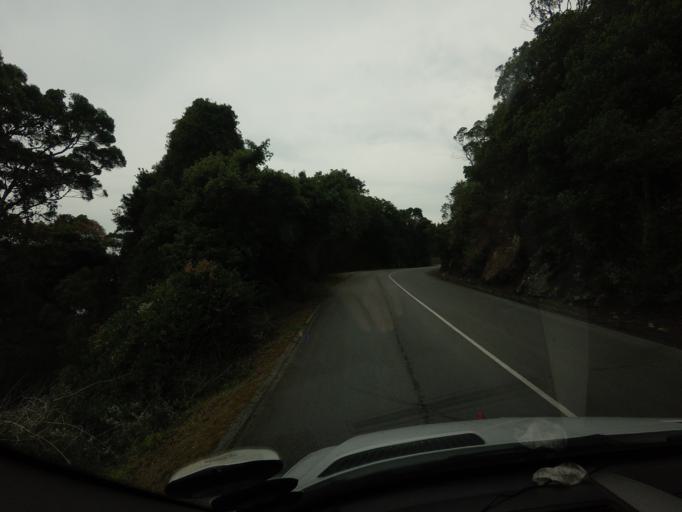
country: ZA
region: Eastern Cape
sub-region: Cacadu District Municipality
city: Kareedouw
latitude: -34.0160
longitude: 23.8750
